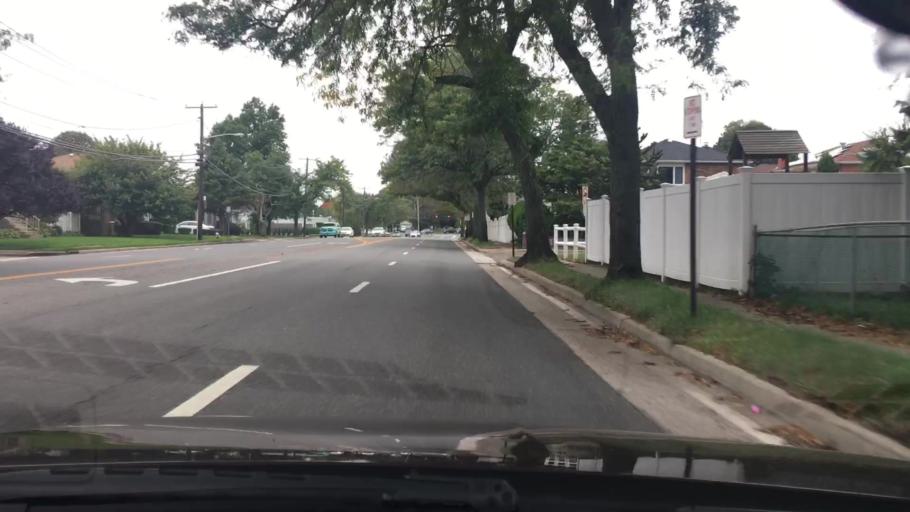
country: US
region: New York
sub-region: Nassau County
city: Bethpage
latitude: 40.7395
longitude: -73.4920
